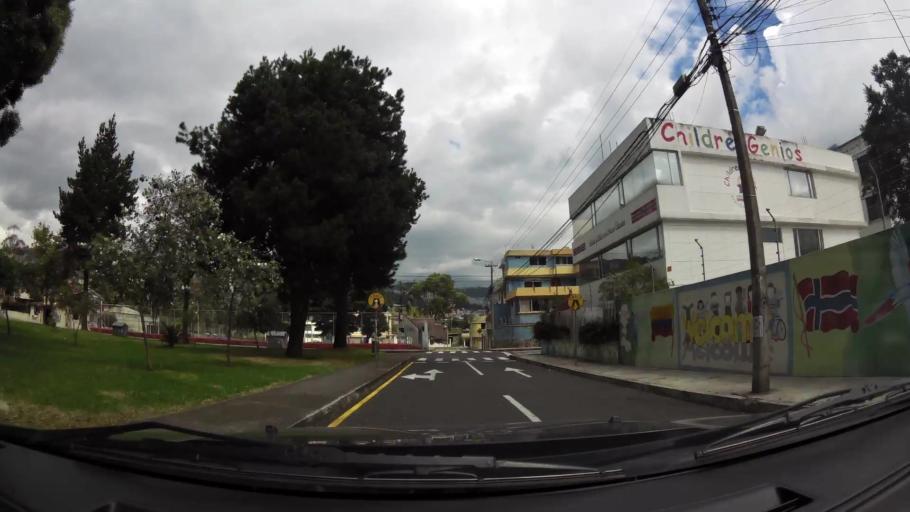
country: EC
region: Pichincha
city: Quito
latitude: -0.2512
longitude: -78.5273
